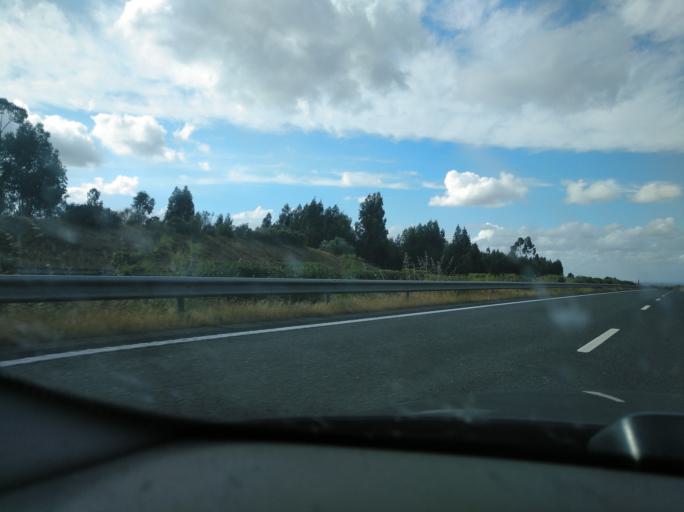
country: PT
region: Beja
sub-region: Aljustrel
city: Aljustrel
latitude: 37.8333
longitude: -8.2303
